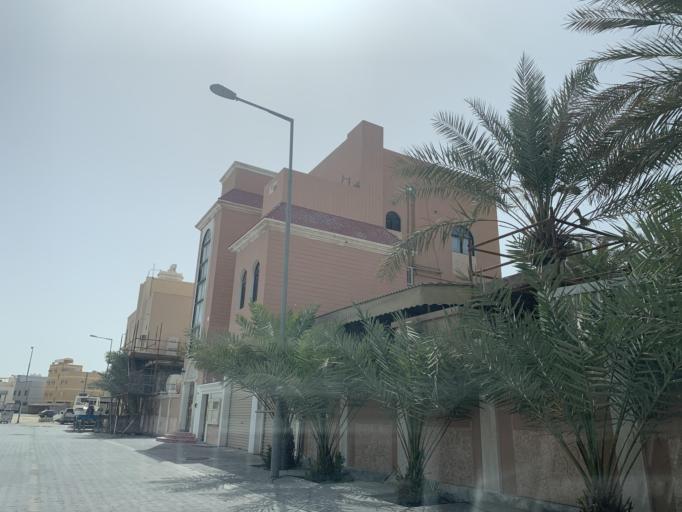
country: BH
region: Northern
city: Sitrah
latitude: 26.1356
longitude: 50.6011
